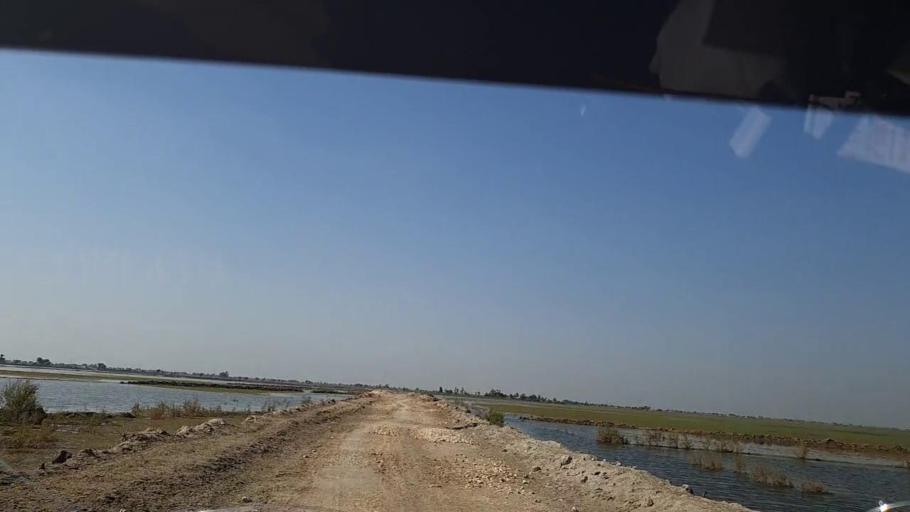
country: PK
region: Sindh
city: Tangwani
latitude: 28.3556
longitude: 69.0385
